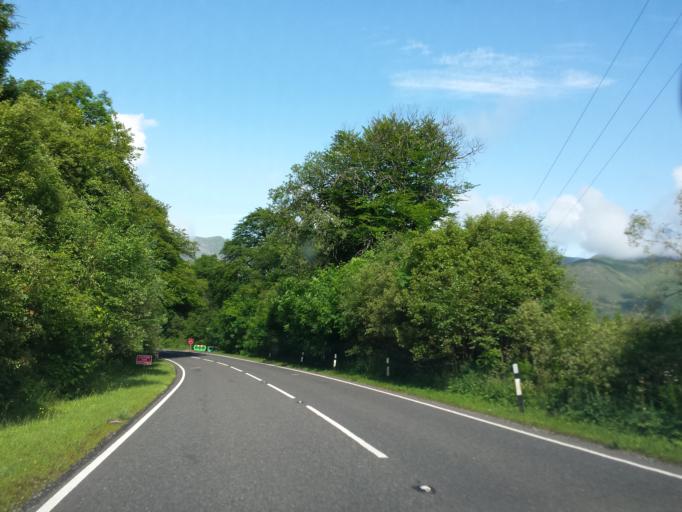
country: GB
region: Scotland
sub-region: Argyll and Bute
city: Garelochhead
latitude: 56.4036
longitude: -4.9981
